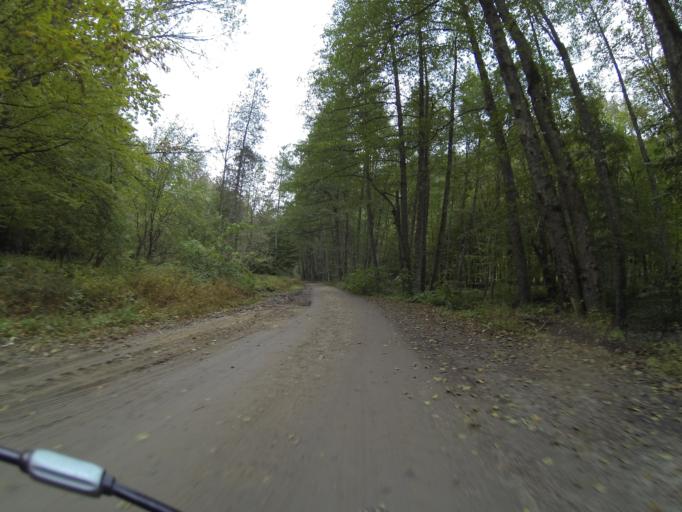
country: RO
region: Gorj
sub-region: Comuna Tismana
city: Sohodol
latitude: 45.0589
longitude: 22.8996
